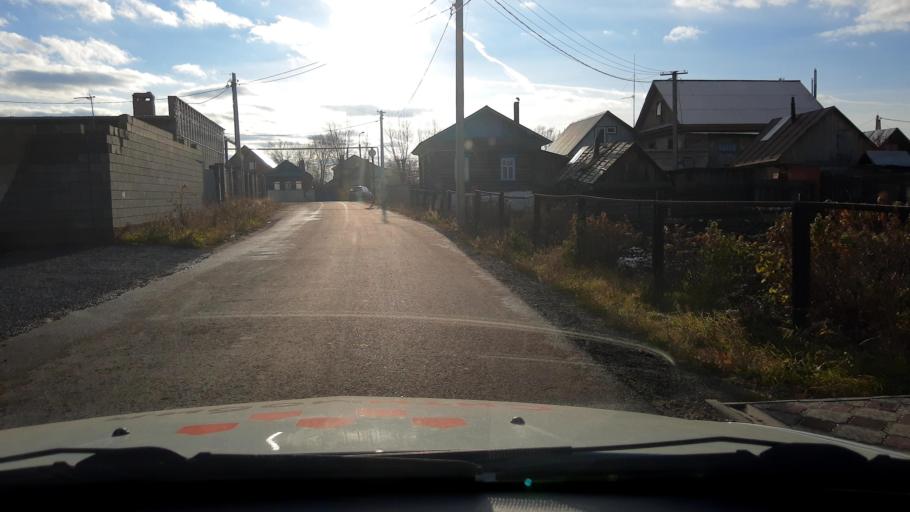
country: RU
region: Bashkortostan
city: Mikhaylovka
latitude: 54.7588
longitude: 55.9064
